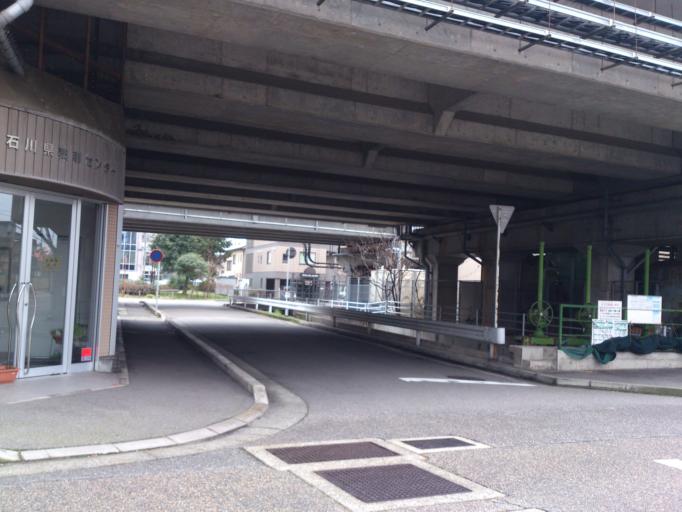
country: JP
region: Ishikawa
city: Kanazawa-shi
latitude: 36.5760
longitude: 136.6460
